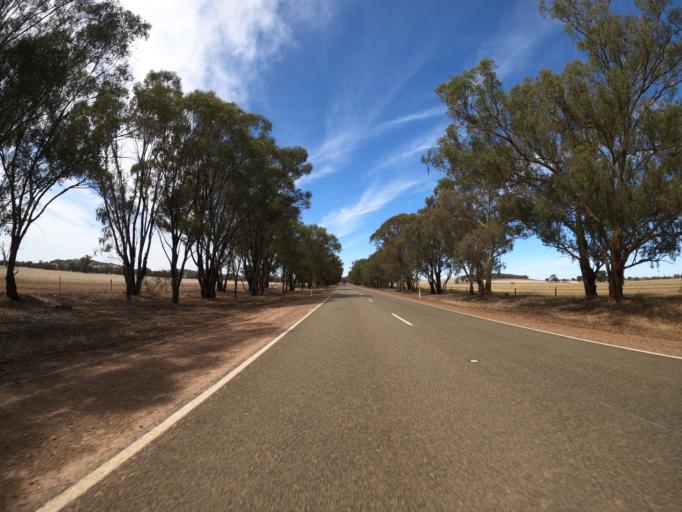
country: AU
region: Victoria
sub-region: Benalla
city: Benalla
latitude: -36.3123
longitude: 145.9583
